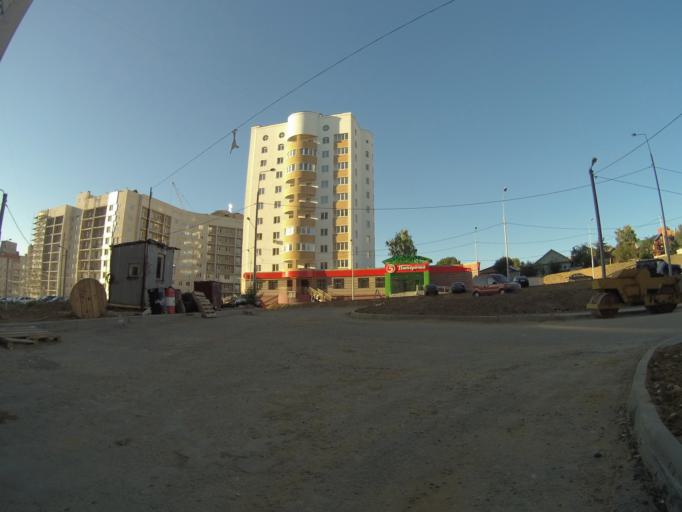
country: RU
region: Vladimir
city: Vladimir
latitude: 56.1065
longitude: 40.3607
